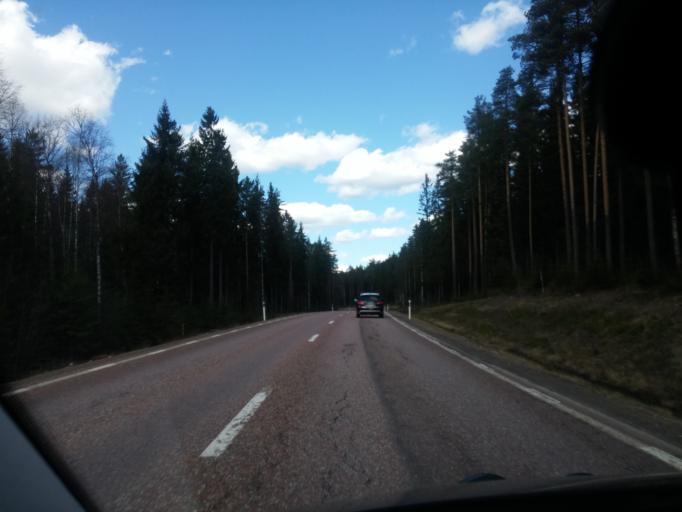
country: SE
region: Dalarna
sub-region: Faluns Kommun
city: Svardsjo
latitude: 60.7706
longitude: 15.7552
